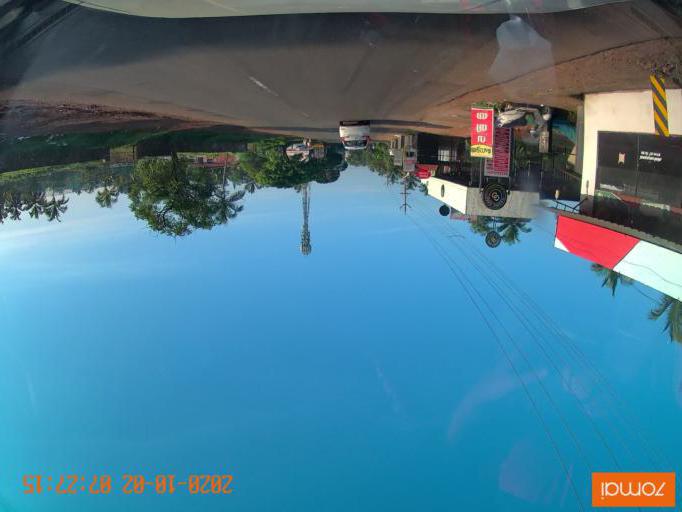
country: IN
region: Kerala
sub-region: Malappuram
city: Pariyapuram
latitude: 11.0220
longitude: 75.9478
